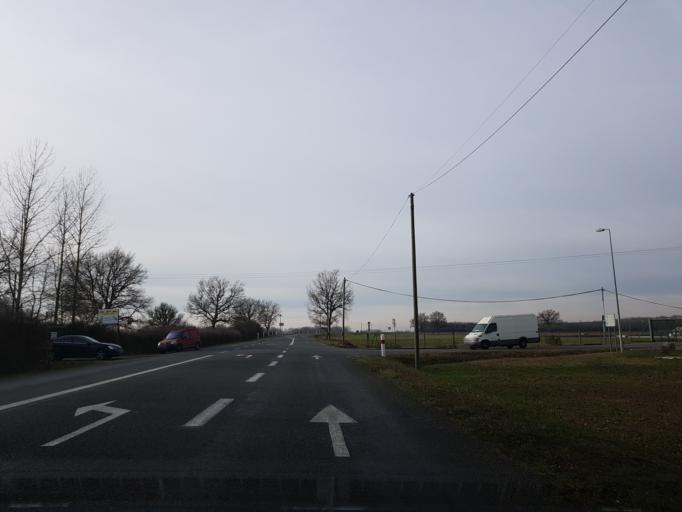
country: FR
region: Auvergne
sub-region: Departement de l'Allier
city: Yzeure
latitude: 46.5777
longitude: 3.4095
